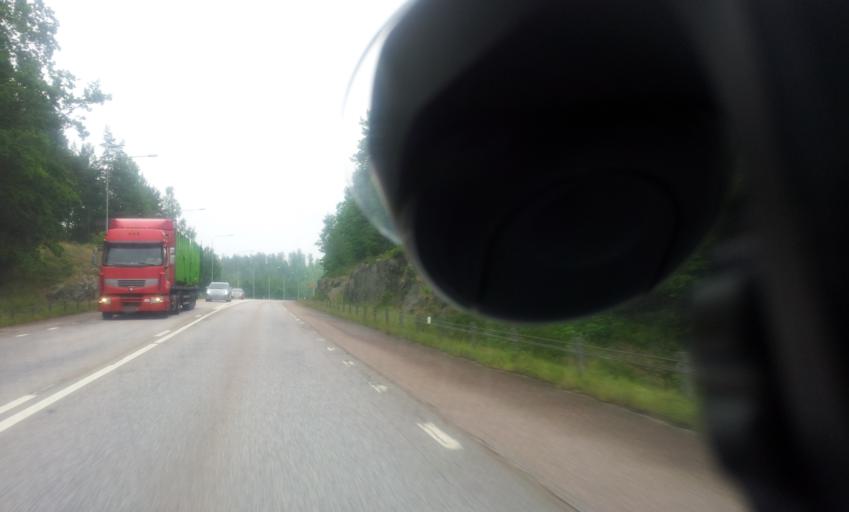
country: SE
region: Kalmar
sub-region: Vasterviks Kommun
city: Ankarsrum
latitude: 57.6646
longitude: 16.4428
